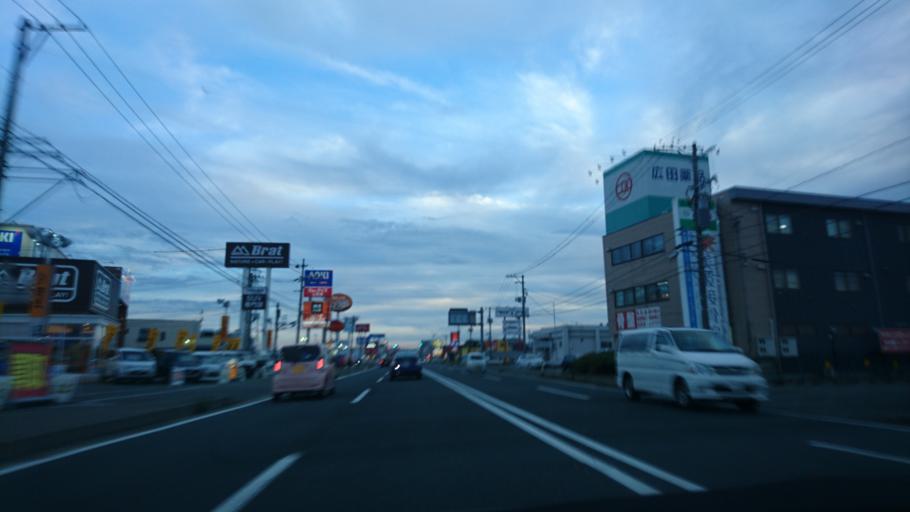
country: JP
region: Iwate
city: Morioka-shi
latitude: 39.6803
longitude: 141.1558
